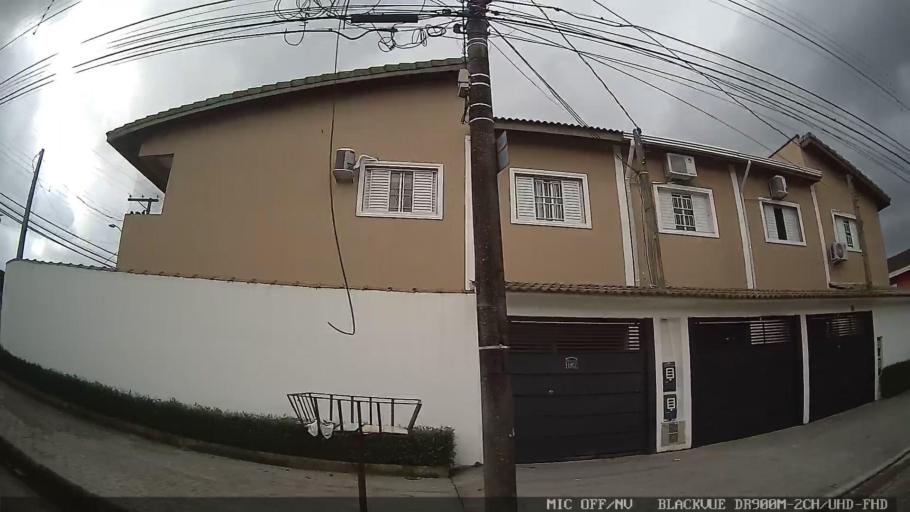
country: BR
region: Sao Paulo
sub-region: Guaruja
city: Guaruja
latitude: -23.9962
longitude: -46.2766
